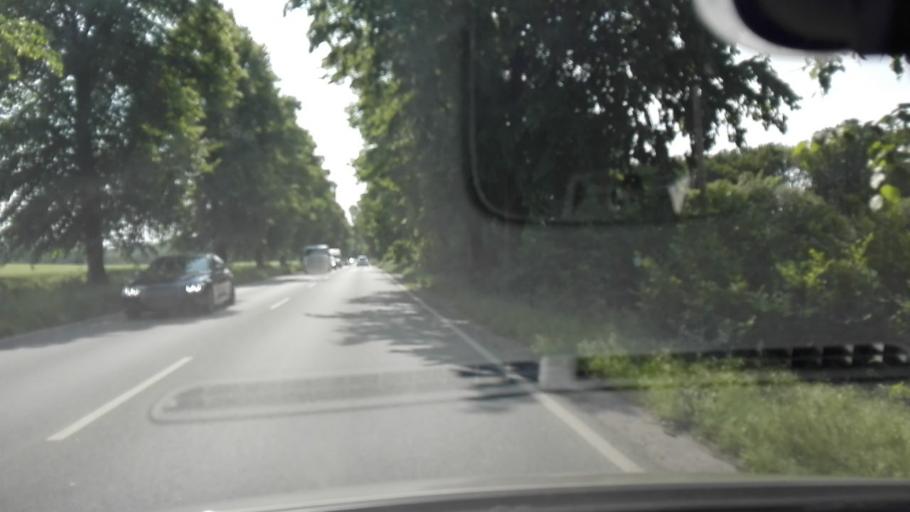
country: DE
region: North Rhine-Westphalia
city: Bergkamen
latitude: 51.5989
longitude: 7.6072
